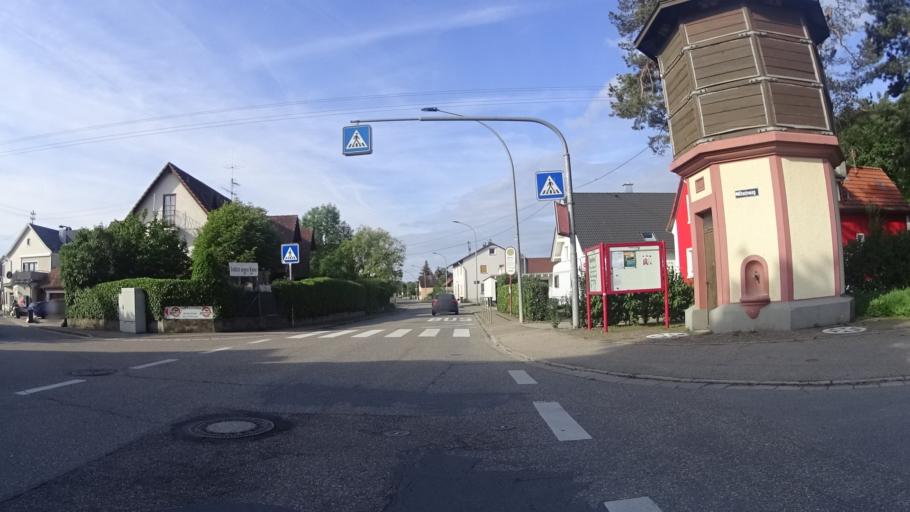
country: DE
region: Baden-Wuerttemberg
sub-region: Freiburg Region
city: Neuenburg am Rhein
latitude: 47.8428
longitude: 7.5776
